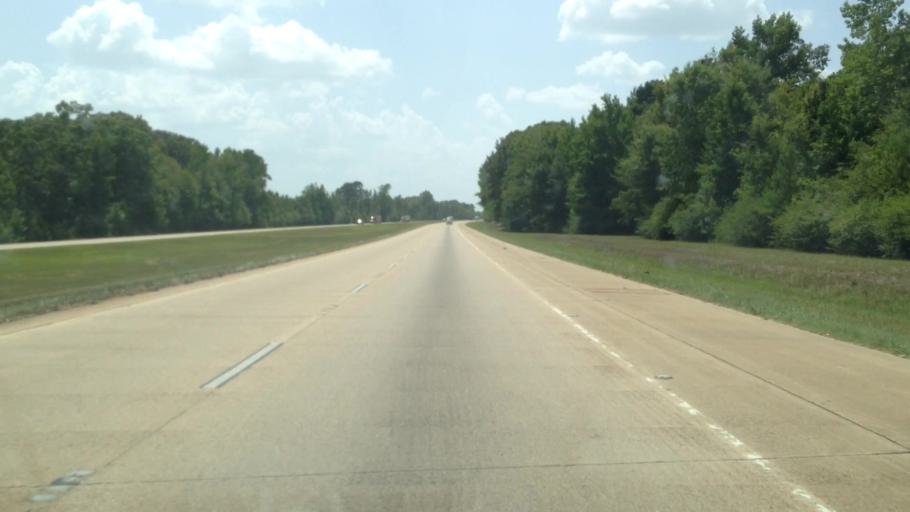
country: US
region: Louisiana
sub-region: Lincoln Parish
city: Grambling
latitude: 32.5407
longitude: -92.6962
